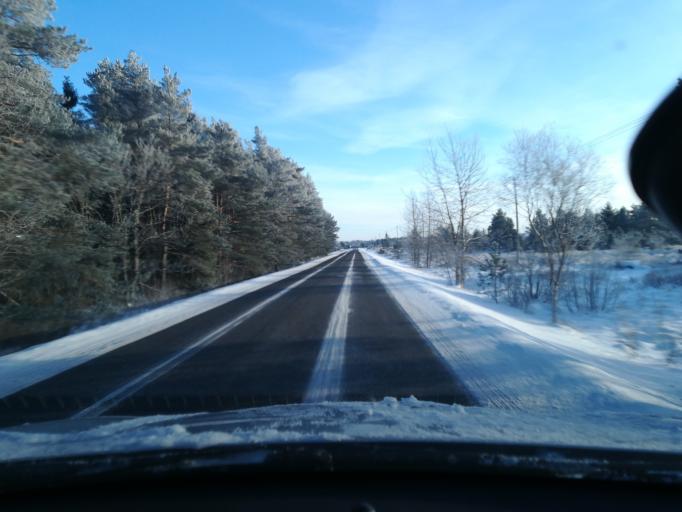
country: EE
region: Harju
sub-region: Keila linn
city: Keila
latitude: 59.3923
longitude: 24.3904
